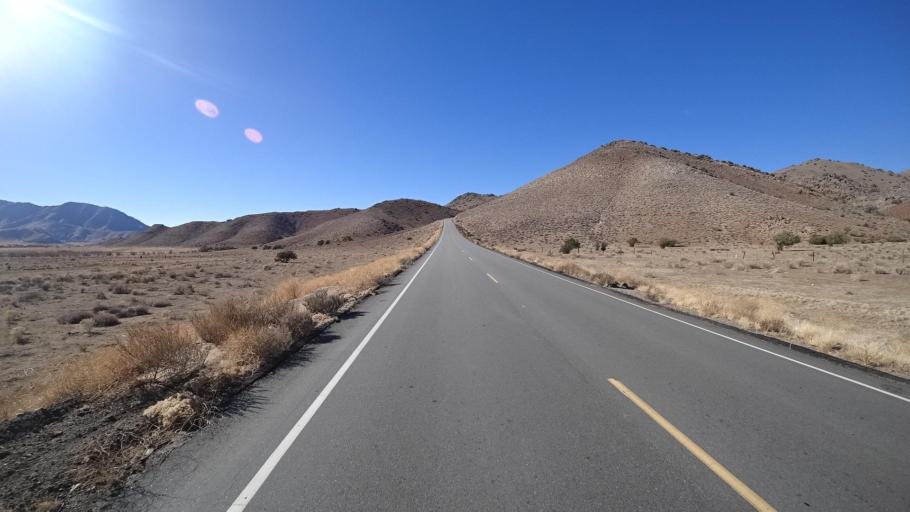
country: US
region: California
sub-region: Kern County
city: Wofford Heights
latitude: 35.6811
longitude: -118.3758
